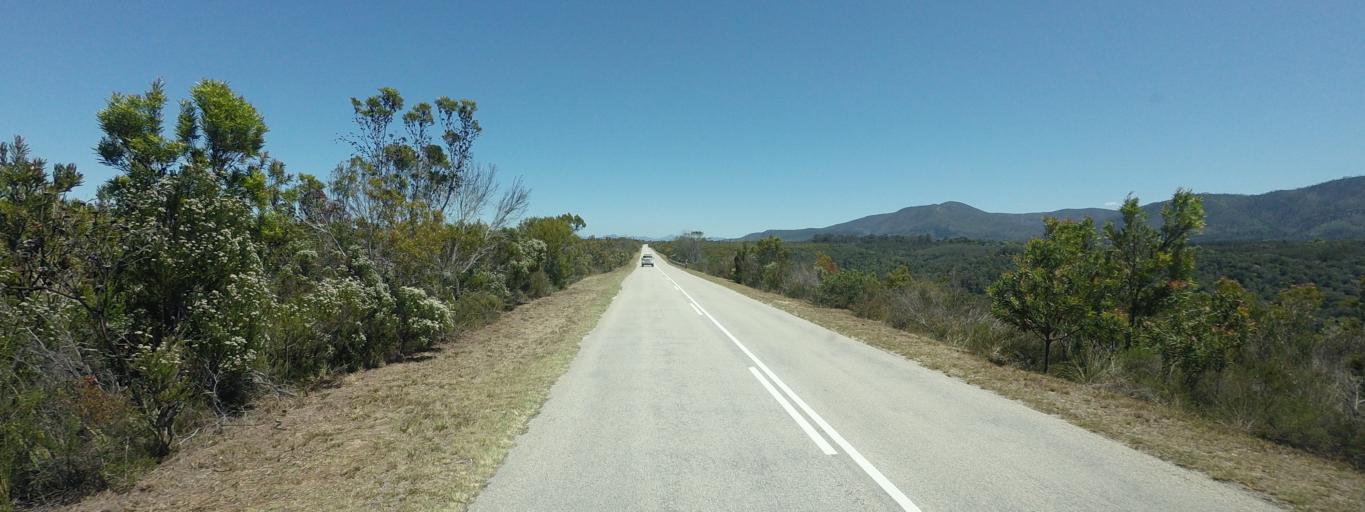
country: ZA
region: Western Cape
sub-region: Eden District Municipality
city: Plettenberg Bay
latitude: -33.9598
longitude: 23.5264
